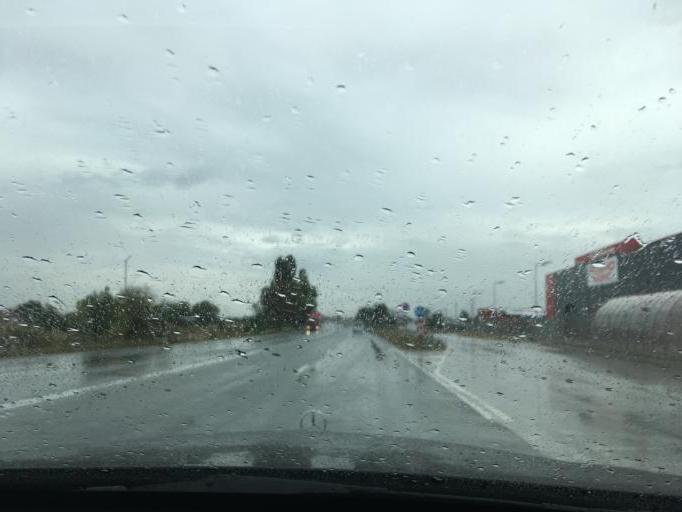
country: BG
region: Sofiya
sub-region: Obshtina Bozhurishte
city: Bozhurishte
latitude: 42.7779
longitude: 23.1772
